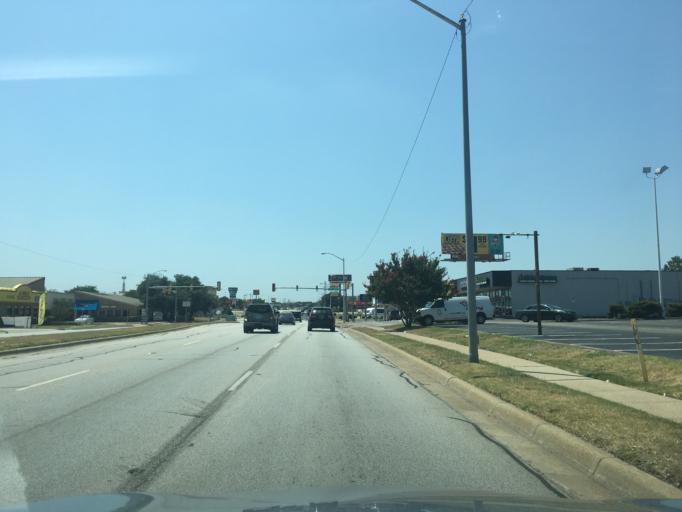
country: US
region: Texas
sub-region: Tarrant County
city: Edgecliff Village
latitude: 32.6542
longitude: -97.3632
